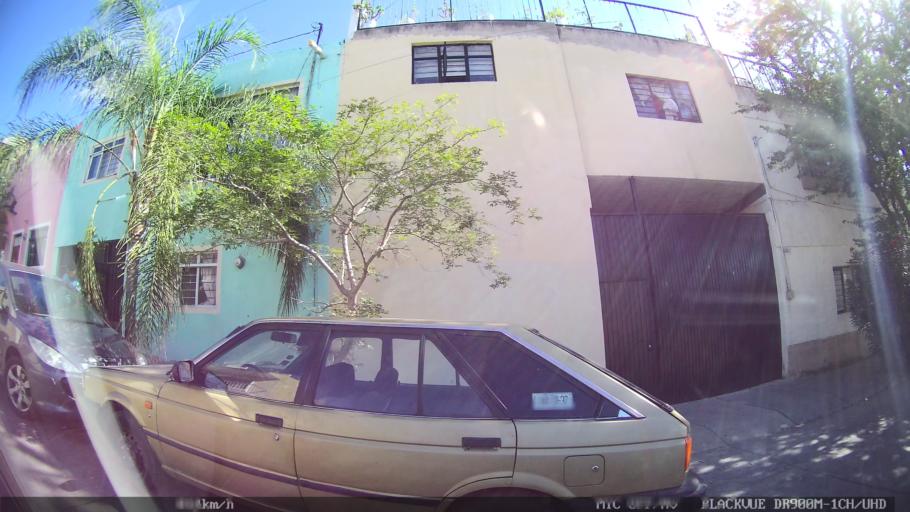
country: MX
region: Jalisco
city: Tlaquepaque
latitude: 20.6850
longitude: -103.2743
